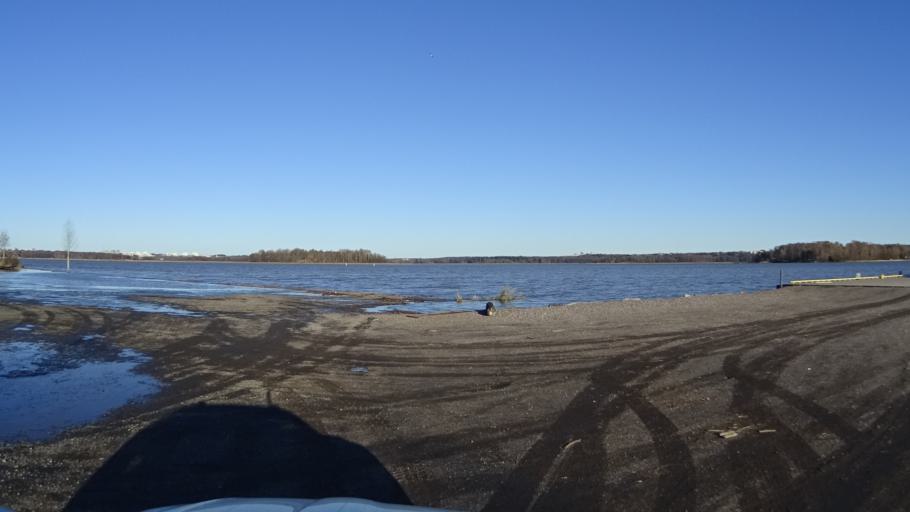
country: FI
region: Uusimaa
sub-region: Helsinki
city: Helsinki
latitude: 60.1956
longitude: 24.9846
